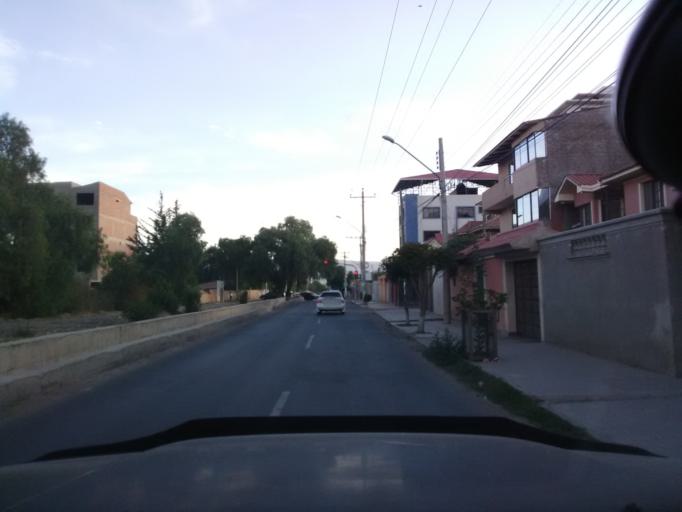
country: BO
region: Cochabamba
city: Cochabamba
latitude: -17.3804
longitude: -66.1990
